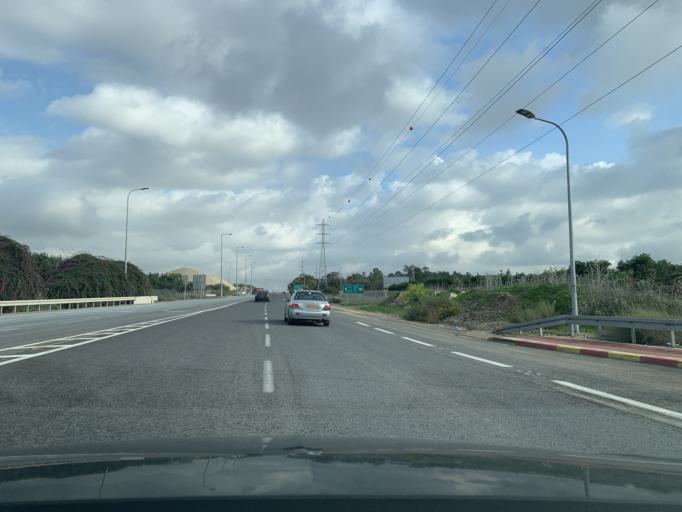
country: IL
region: Central District
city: Rosh Ha'Ayin
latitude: 32.0674
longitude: 34.9446
